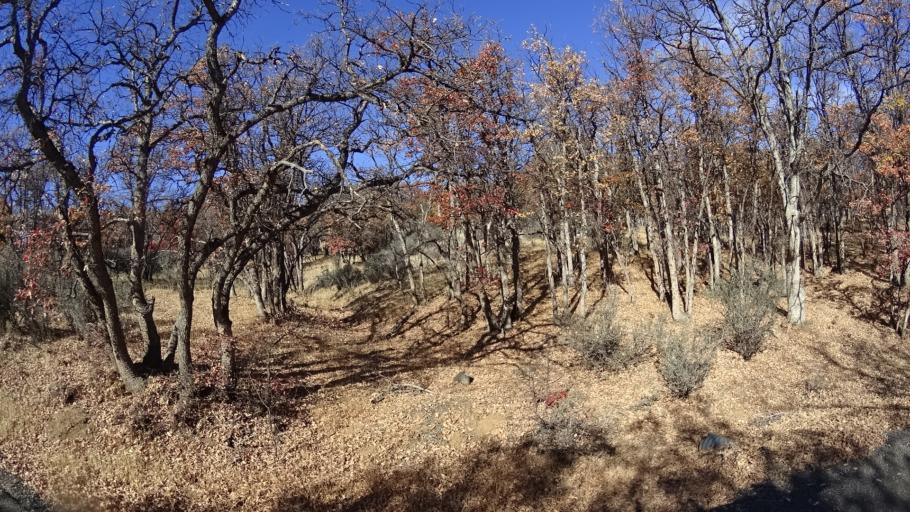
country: US
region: California
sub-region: Siskiyou County
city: Yreka
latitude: 41.7731
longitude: -122.6430
